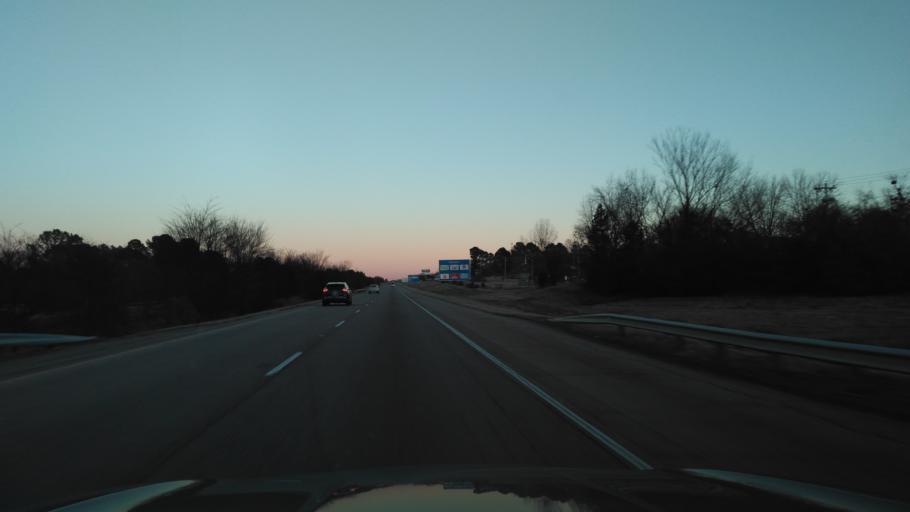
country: US
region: Arkansas
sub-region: Crawford County
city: Van Buren
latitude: 35.4652
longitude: -94.3758
